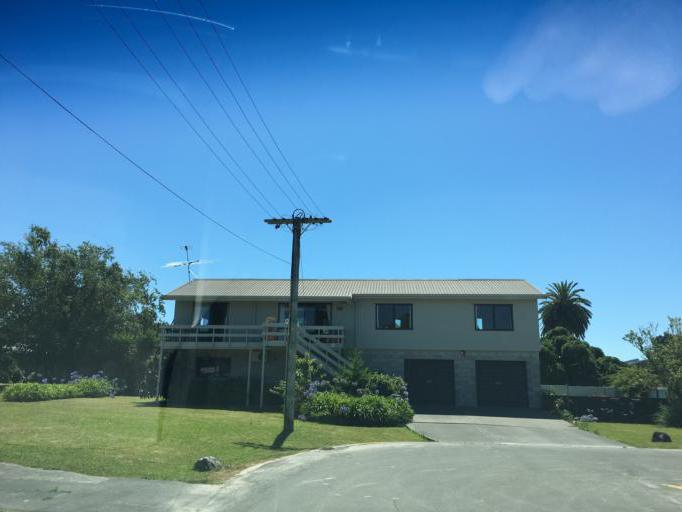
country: NZ
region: Gisborne
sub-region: Gisborne District
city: Gisborne
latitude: -38.6585
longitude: 178.0240
